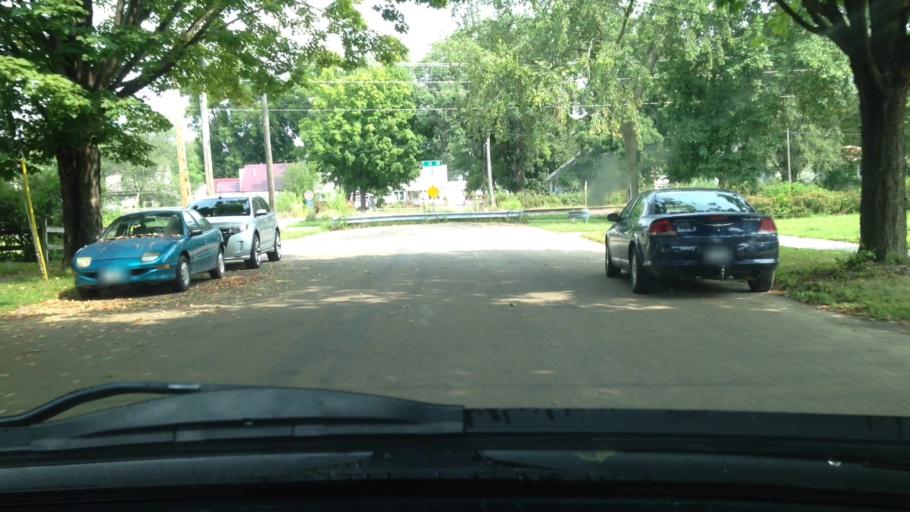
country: US
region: Minnesota
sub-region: Olmsted County
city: Rochester
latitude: 44.0243
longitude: -92.4461
